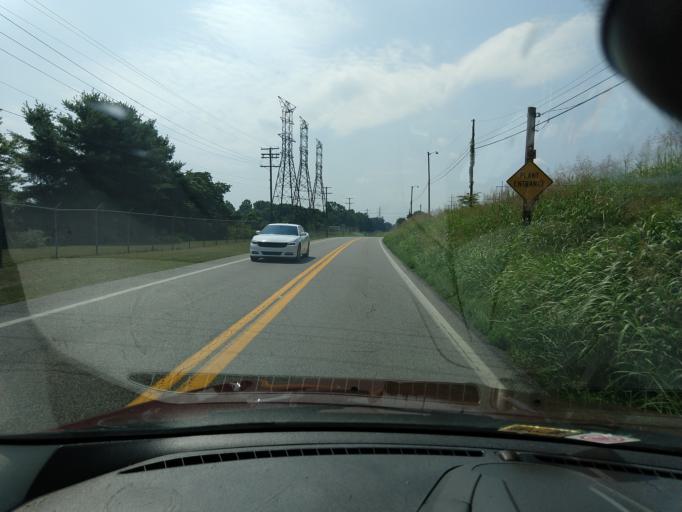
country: US
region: West Virginia
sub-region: Mason County
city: New Haven
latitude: 38.9665
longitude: -81.9289
